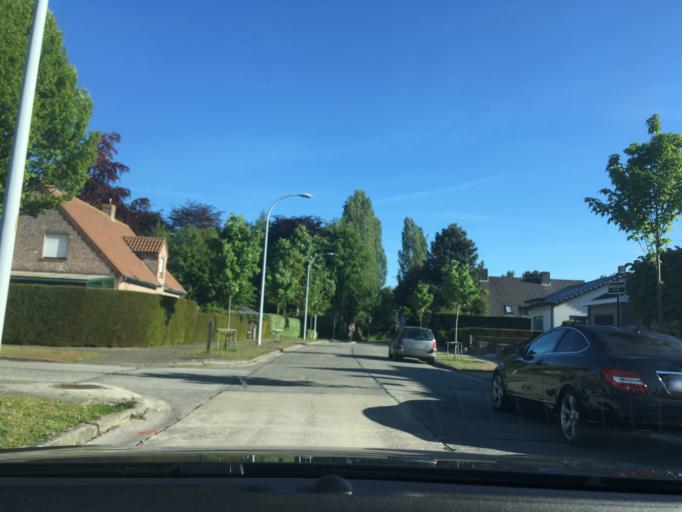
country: BE
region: Flanders
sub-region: Provincie West-Vlaanderen
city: Oostkamp
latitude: 51.1790
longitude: 3.2151
